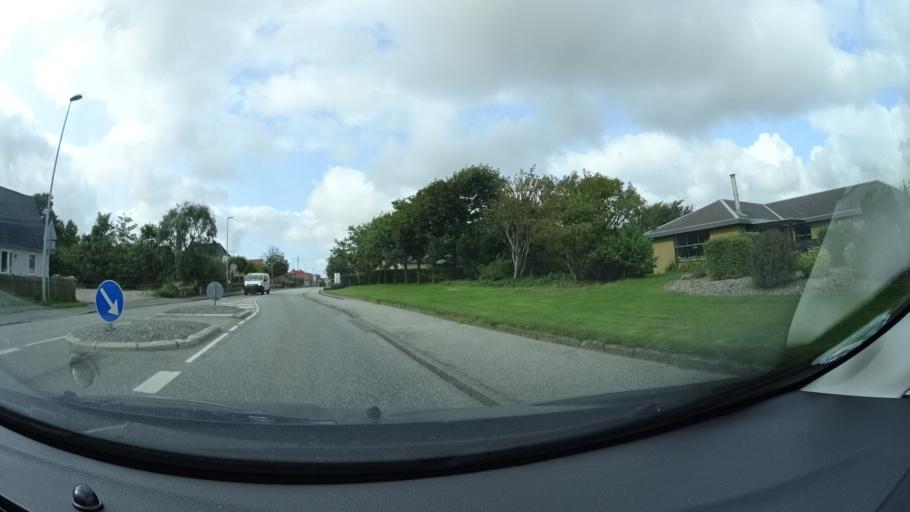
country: DK
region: Central Jutland
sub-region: Lemvig Kommune
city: Harboore
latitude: 56.5635
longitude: 8.2231
